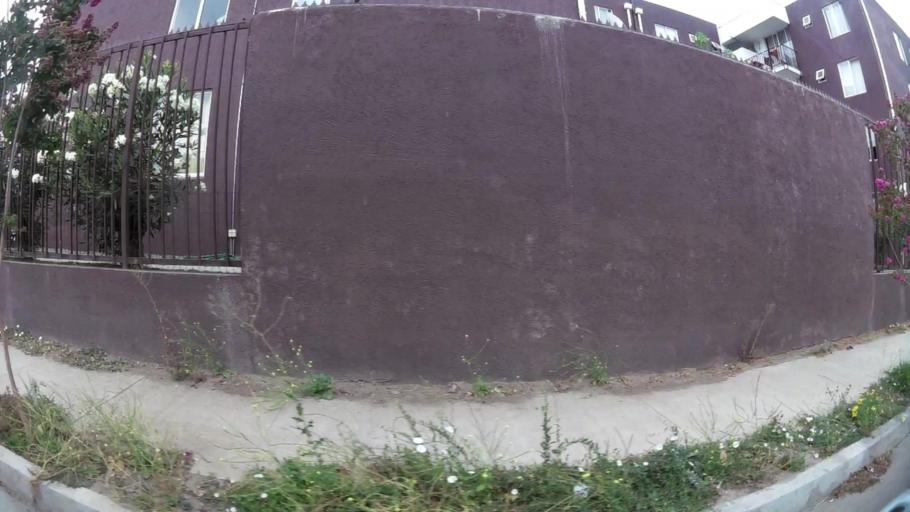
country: CL
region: O'Higgins
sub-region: Provincia de Cachapoal
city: Rancagua
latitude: -34.1418
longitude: -70.7415
